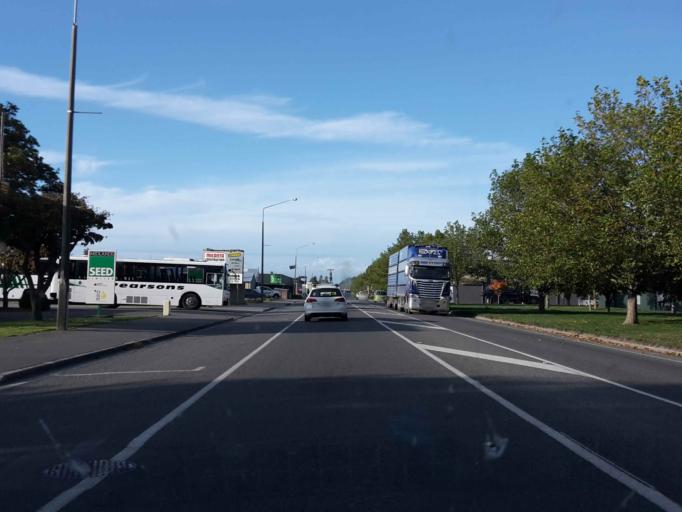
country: NZ
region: Canterbury
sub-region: Ashburton District
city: Ashburton
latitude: -43.8960
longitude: 171.7591
